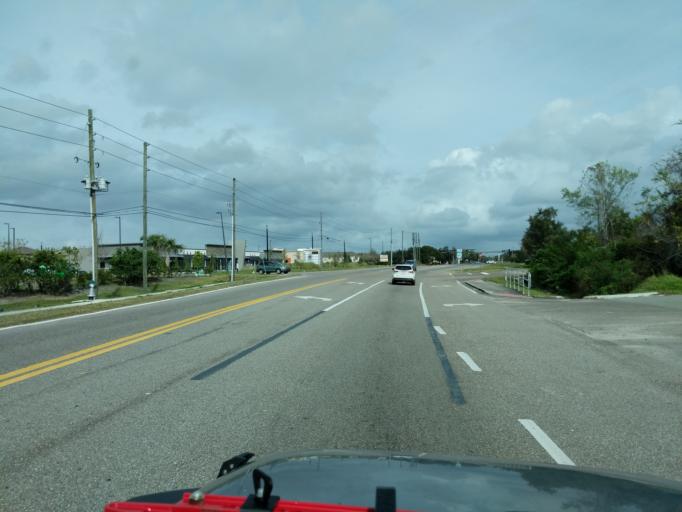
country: US
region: Florida
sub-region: Orange County
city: Paradise Heights
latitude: 28.6009
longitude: -81.5532
